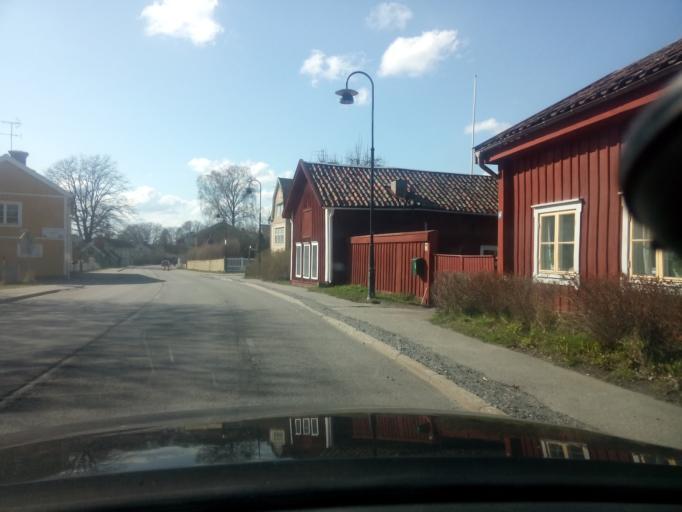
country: SE
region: Soedermanland
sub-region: Flens Kommun
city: Malmkoping
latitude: 59.1312
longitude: 16.7340
